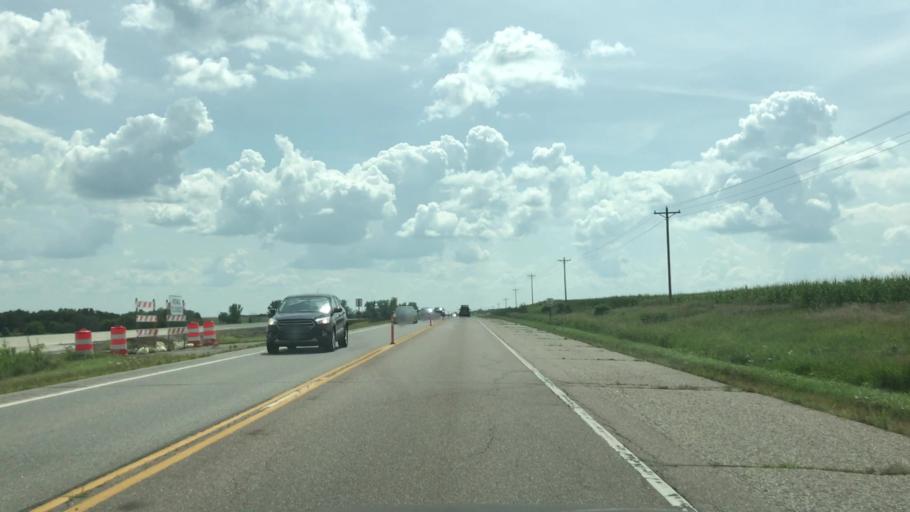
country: US
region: Minnesota
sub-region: Scott County
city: Belle Plaine
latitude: 44.5696
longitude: -93.8446
